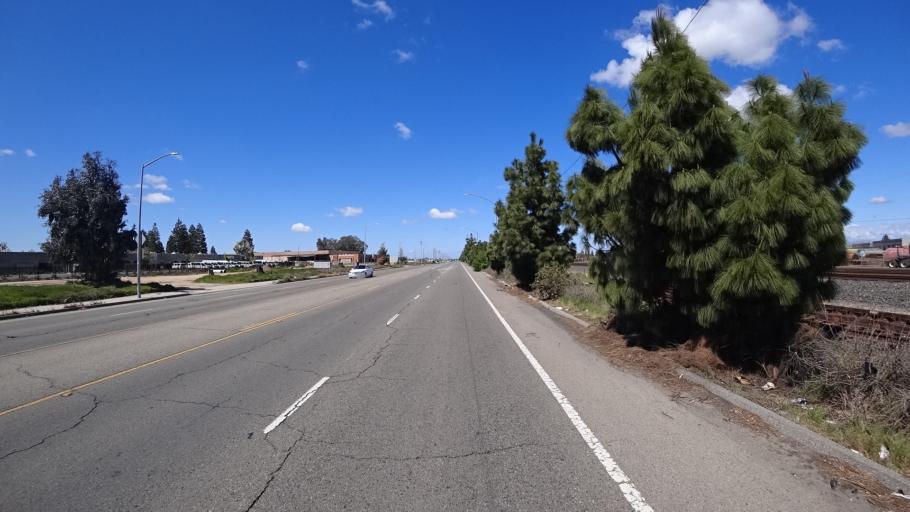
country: US
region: California
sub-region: Fresno County
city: West Park
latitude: 36.7965
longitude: -119.8645
